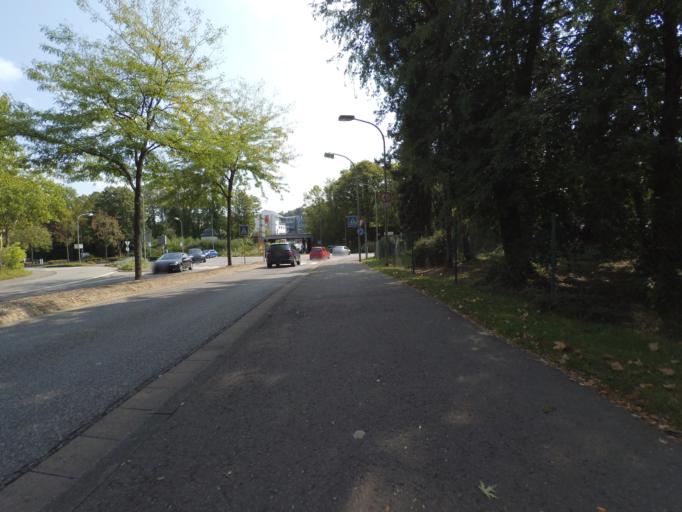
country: DE
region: Saarland
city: Merzig
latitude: 49.4406
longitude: 6.6330
